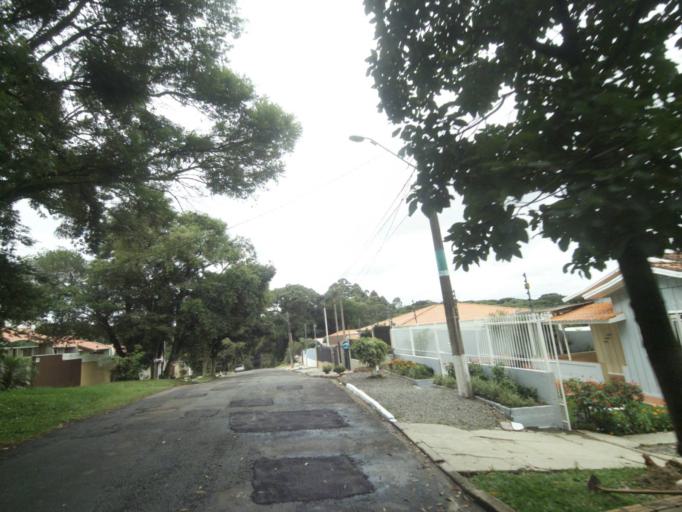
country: BR
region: Parana
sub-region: Curitiba
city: Curitiba
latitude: -25.4504
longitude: -49.3308
